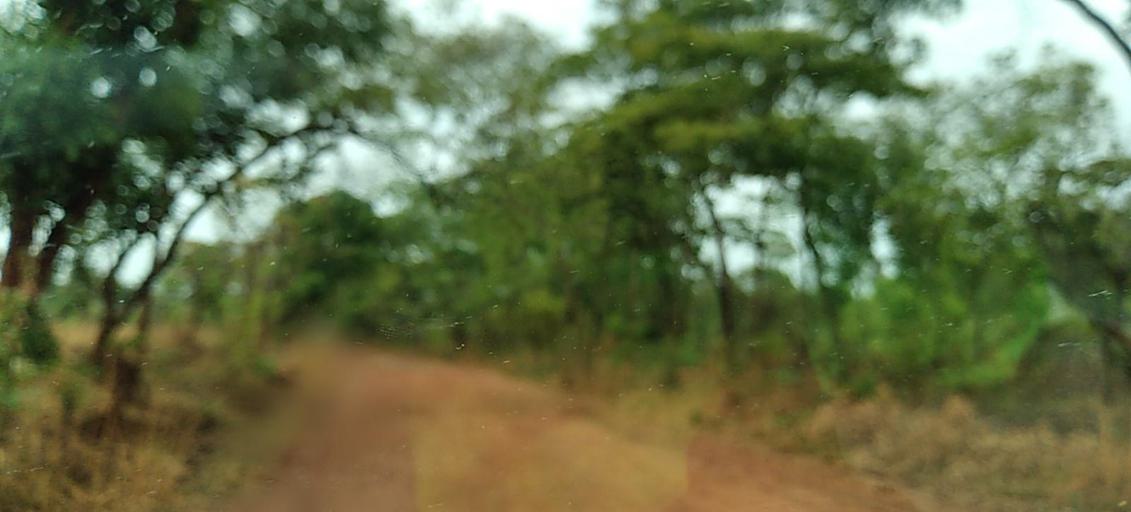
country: ZM
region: North-Western
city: Solwezi
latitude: -12.3191
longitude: 26.5220
